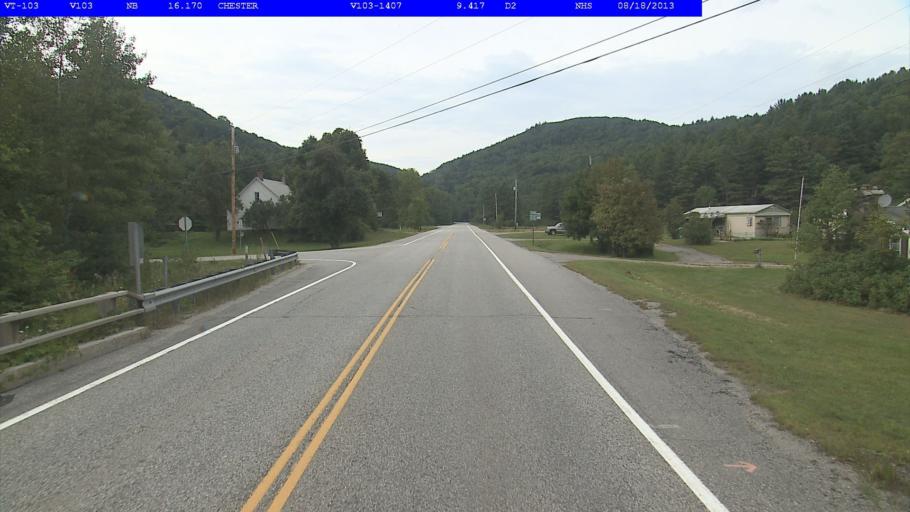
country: US
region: Vermont
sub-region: Windsor County
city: Chester
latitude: 43.3452
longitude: -72.6232
